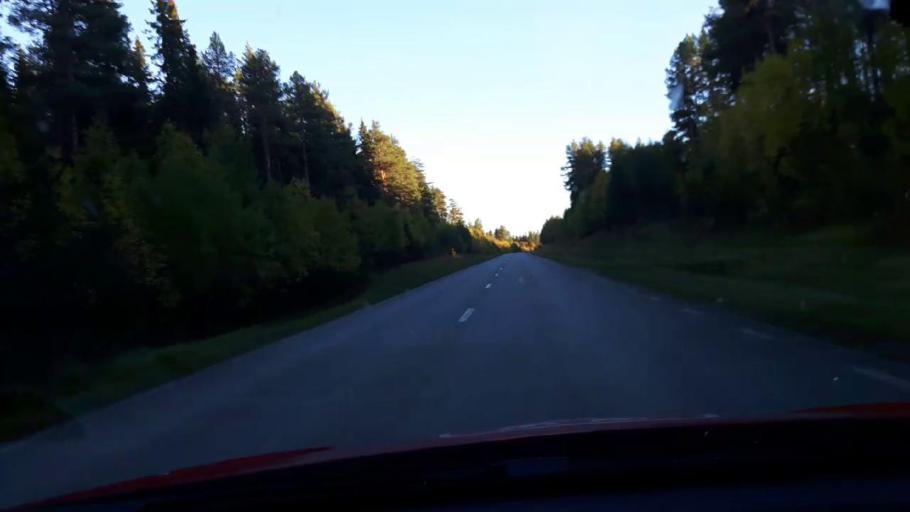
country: SE
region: Jaemtland
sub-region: Krokoms Kommun
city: Krokom
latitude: 63.4402
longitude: 14.4960
